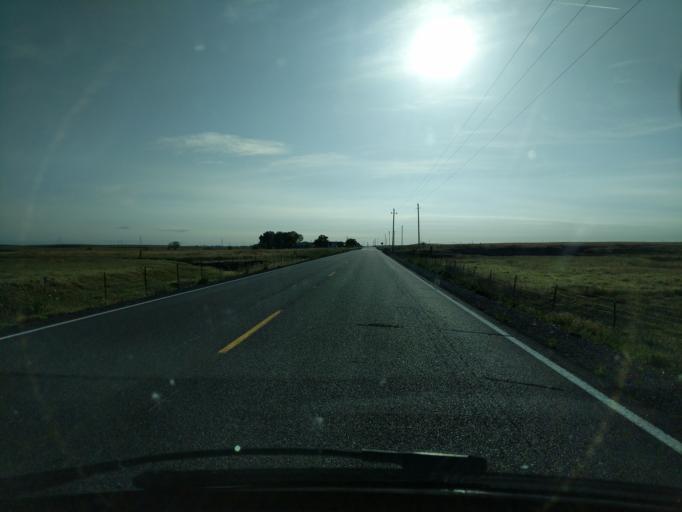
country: US
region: California
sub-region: San Joaquin County
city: Escalon
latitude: 37.9449
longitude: -120.9342
